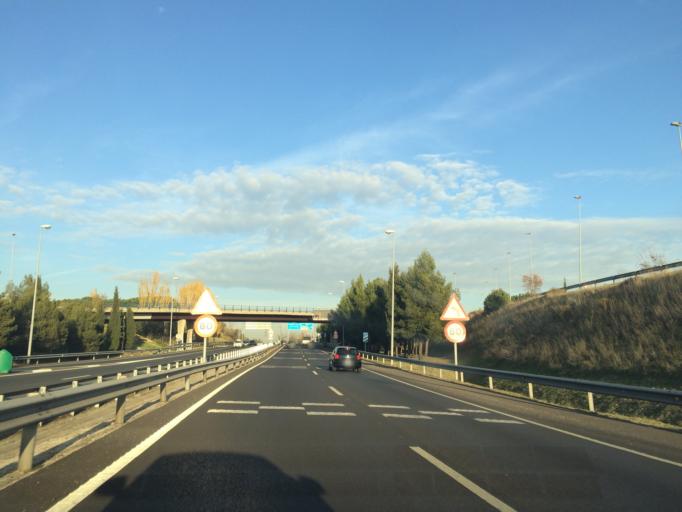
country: ES
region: Madrid
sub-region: Provincia de Madrid
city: Las Tablas
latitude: 40.5099
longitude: -3.6886
